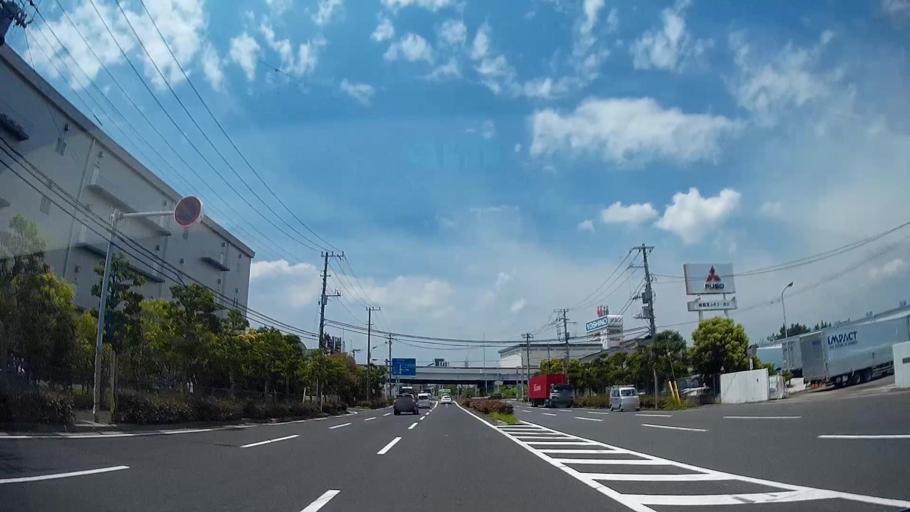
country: JP
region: Tokyo
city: Urayasu
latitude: 35.6599
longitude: 139.9172
